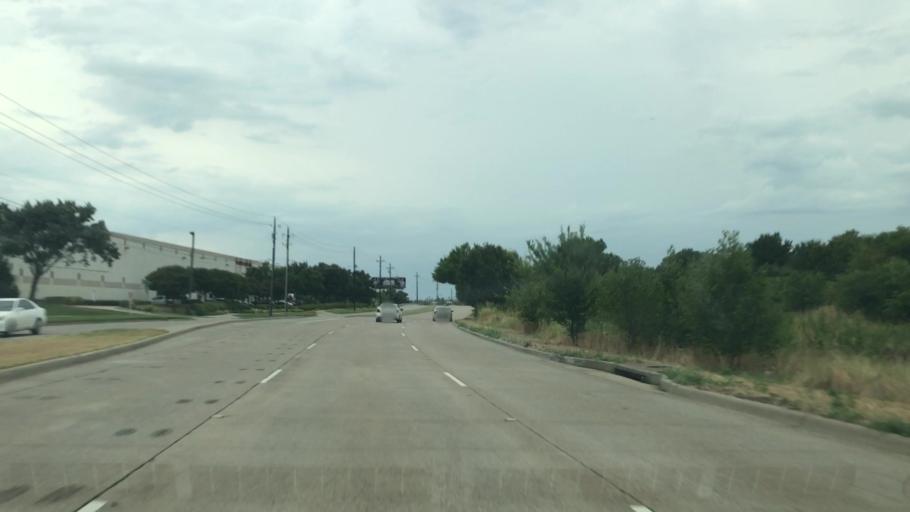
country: US
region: Texas
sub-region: Dallas County
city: Carrollton
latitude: 32.9513
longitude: -96.9355
